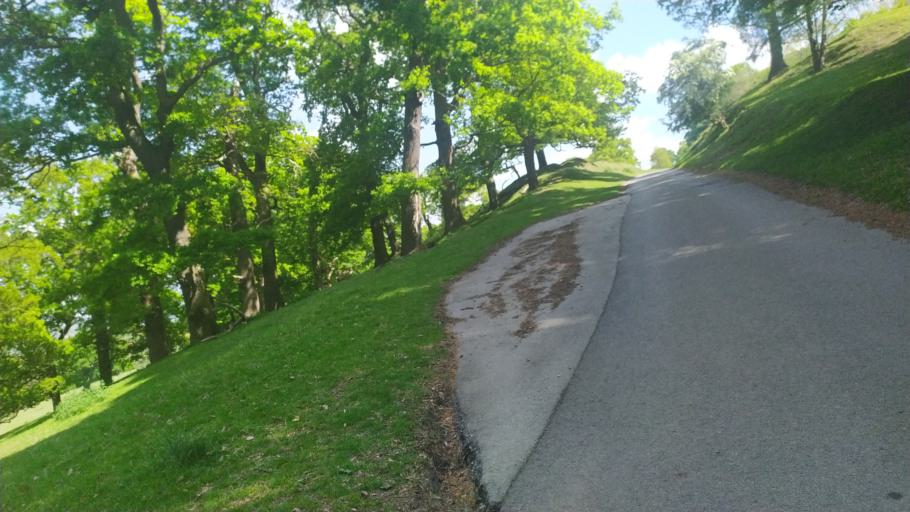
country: GB
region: England
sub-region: North Yorkshire
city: Pannal
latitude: 53.9007
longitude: -1.5333
